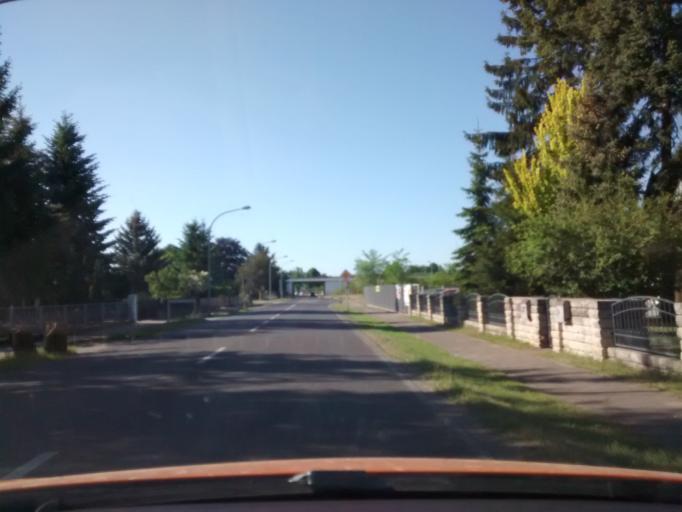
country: DE
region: Brandenburg
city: Langewahl
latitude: 52.3325
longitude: 14.0762
